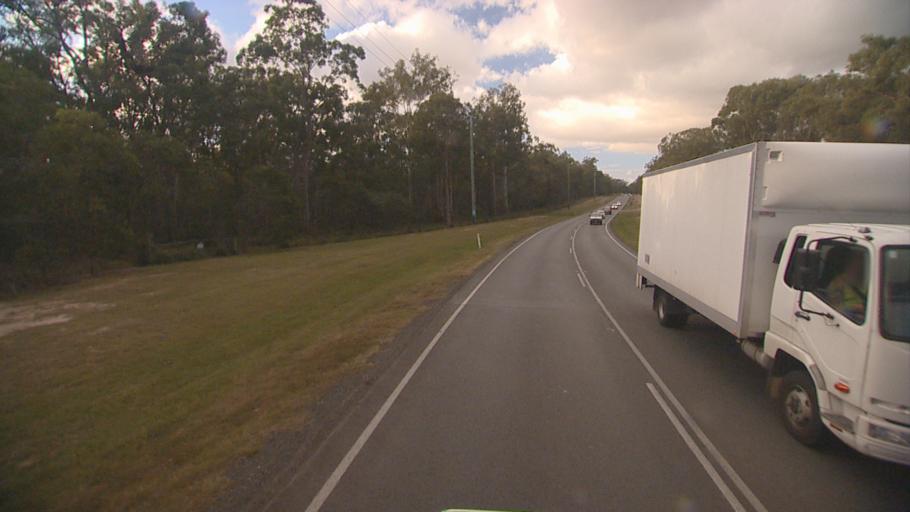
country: AU
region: Queensland
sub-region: Logan
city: Park Ridge South
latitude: -27.7139
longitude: 152.9941
